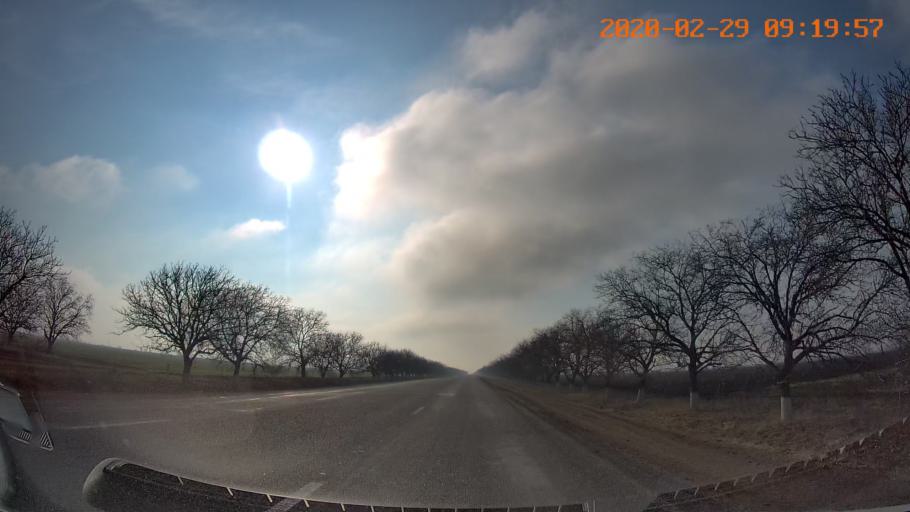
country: MD
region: Telenesti
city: Pervomaisc
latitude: 46.7558
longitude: 29.9440
